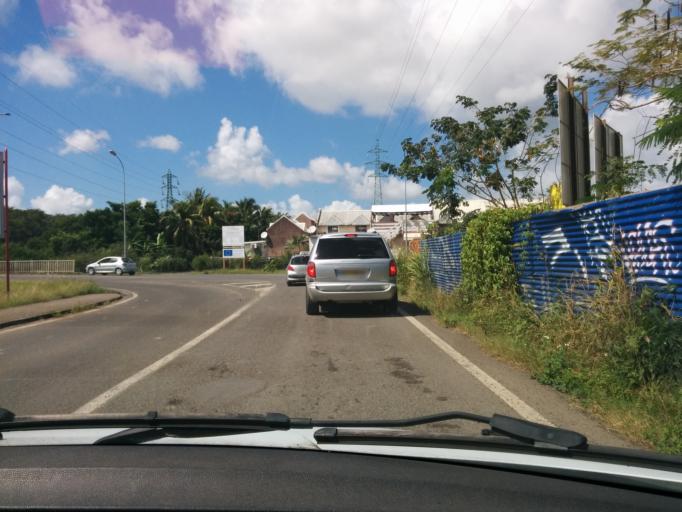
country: GP
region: Guadeloupe
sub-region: Guadeloupe
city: Pointe-a-Pitre
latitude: 16.2550
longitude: -61.5330
